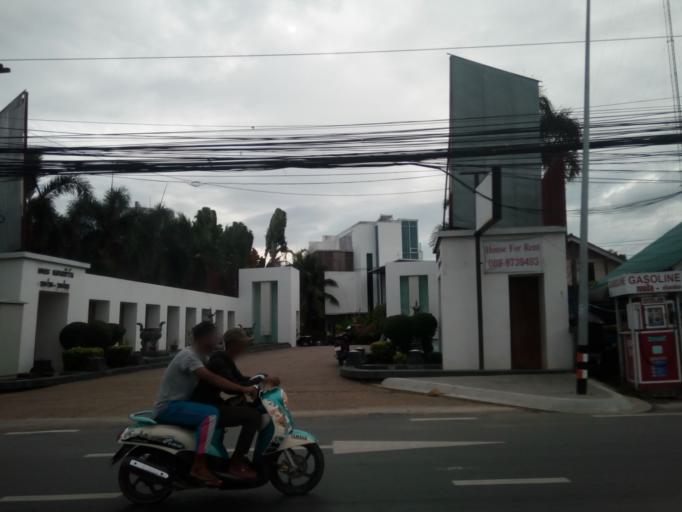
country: TH
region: Phuket
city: Ban Ko Kaeo
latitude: 7.9609
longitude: 98.3813
